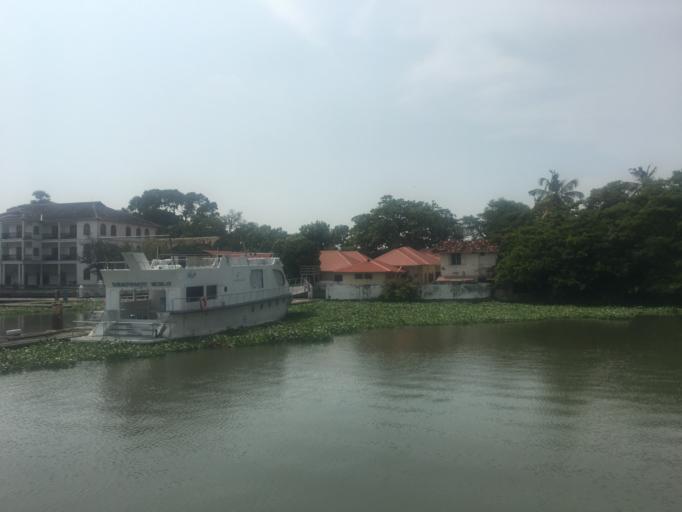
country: IN
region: Kerala
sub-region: Ernakulam
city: Cochin
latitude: 9.9861
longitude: 76.2683
